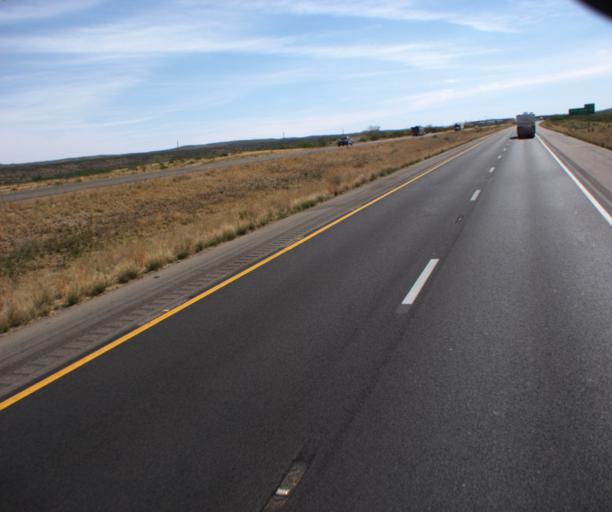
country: US
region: Arizona
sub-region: Cochise County
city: Mescal
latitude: 31.9839
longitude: -110.5523
